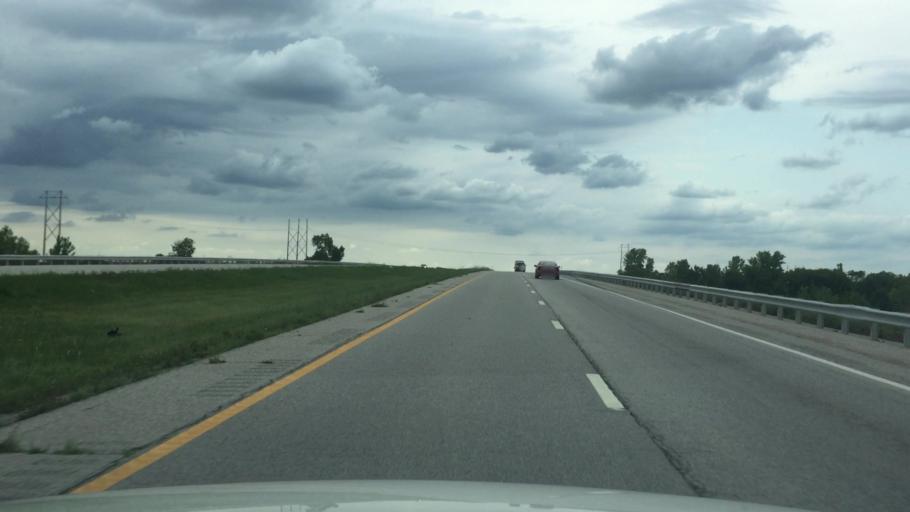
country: US
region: Kansas
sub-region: Miami County
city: Louisburg
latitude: 38.7426
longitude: -94.6764
